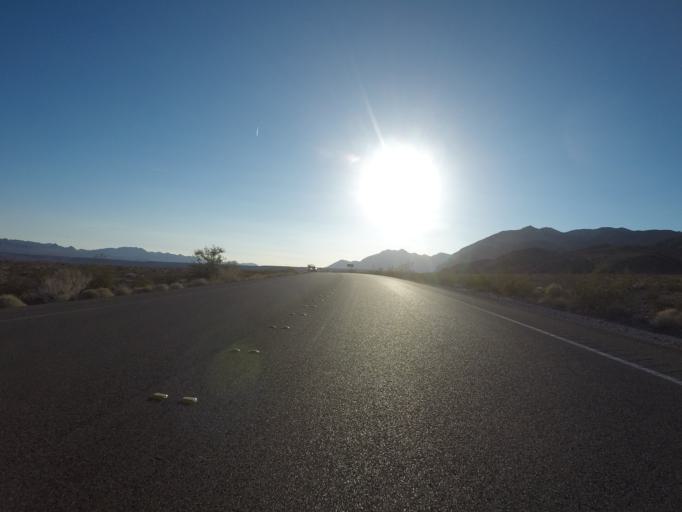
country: US
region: Nevada
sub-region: Clark County
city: Moapa Valley
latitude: 36.3796
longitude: -114.4391
